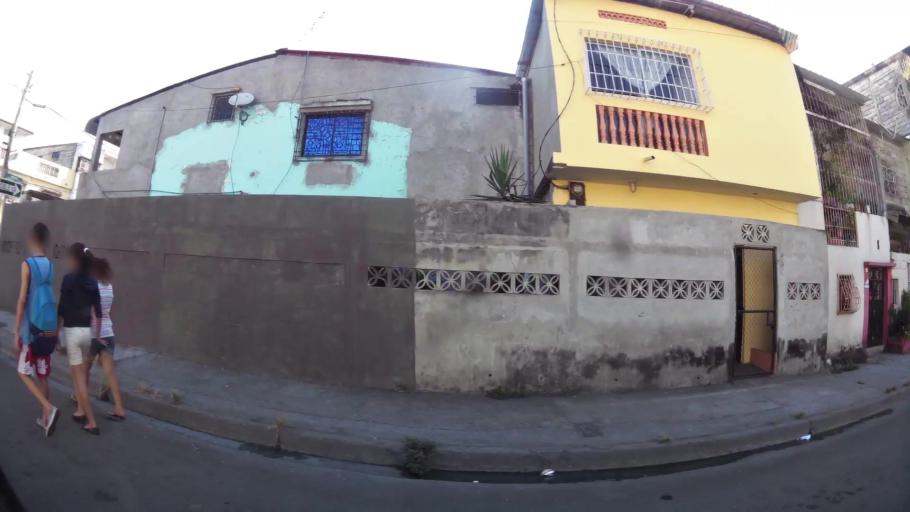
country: EC
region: Guayas
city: Guayaquil
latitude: -2.2066
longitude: -79.9233
